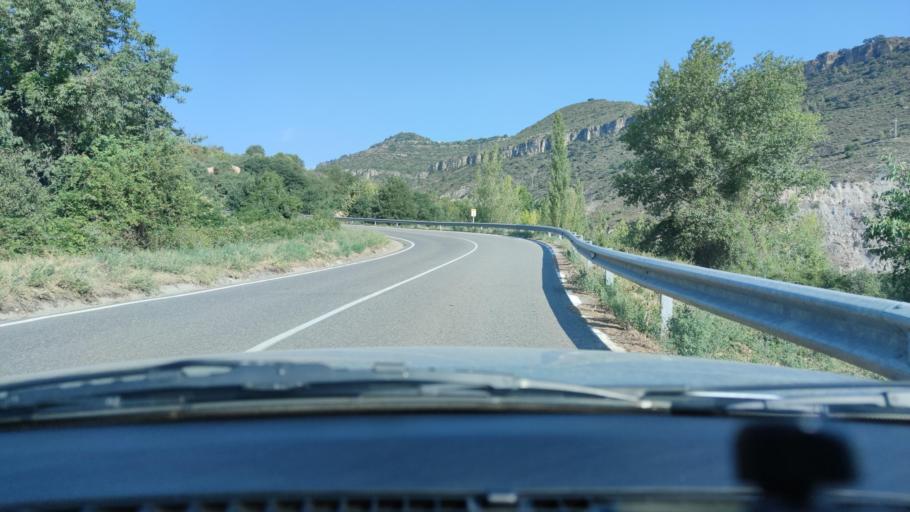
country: ES
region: Catalonia
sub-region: Provincia de Lleida
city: Llimiana
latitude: 42.0951
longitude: 0.8790
